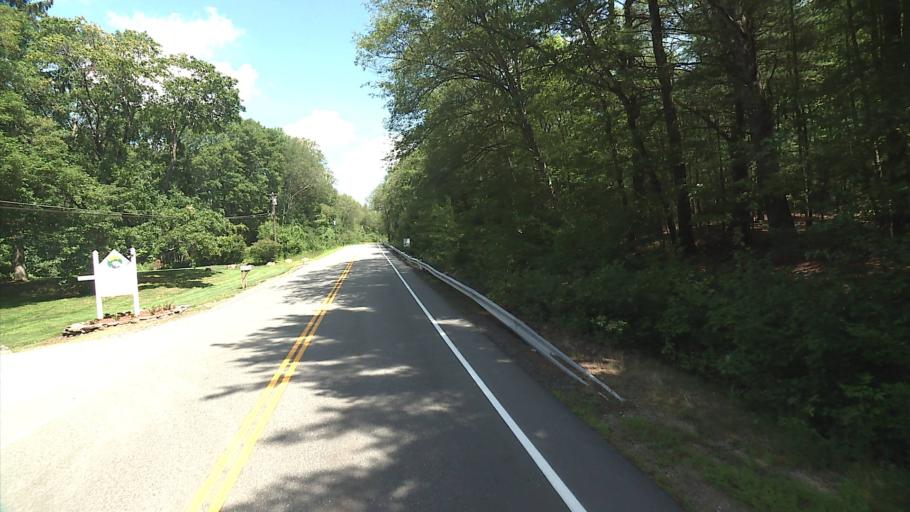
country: US
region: Massachusetts
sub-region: Worcester County
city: Southbridge
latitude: 42.0065
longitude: -72.0819
